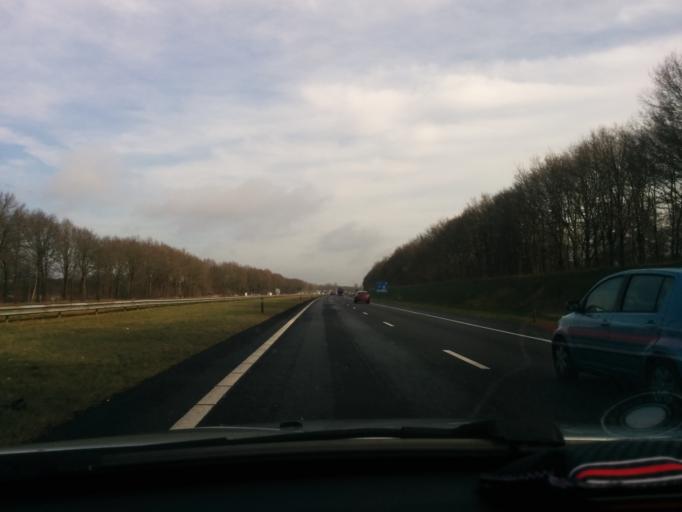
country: NL
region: North Holland
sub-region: Gemeente Blaricum
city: Blaricum
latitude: 52.2568
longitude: 5.2504
